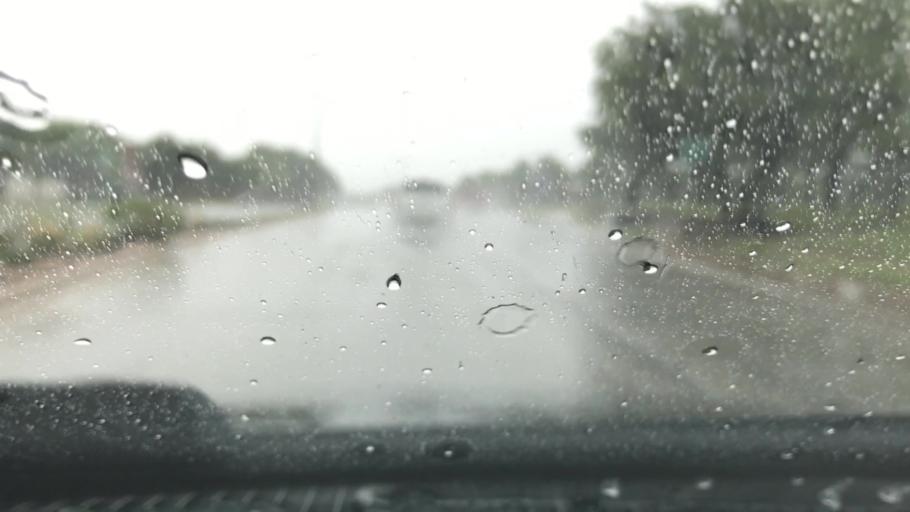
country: US
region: Texas
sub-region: Williamson County
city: Leander
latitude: 30.5326
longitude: -97.8594
